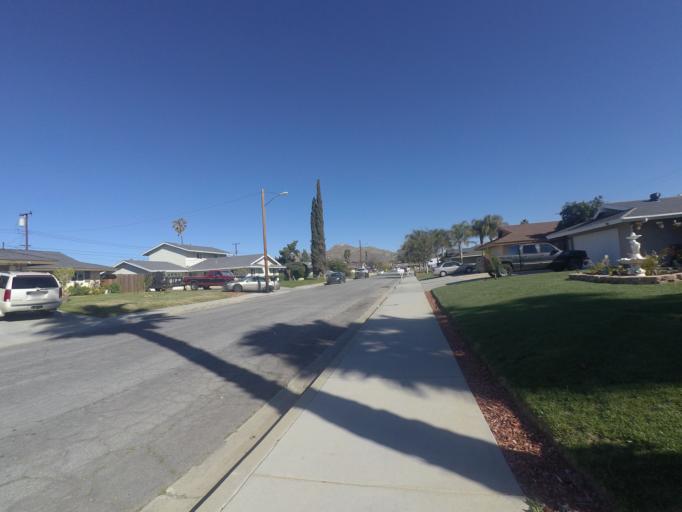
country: US
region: California
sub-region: Riverside County
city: March Air Force Base
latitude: 33.9211
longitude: -117.2682
